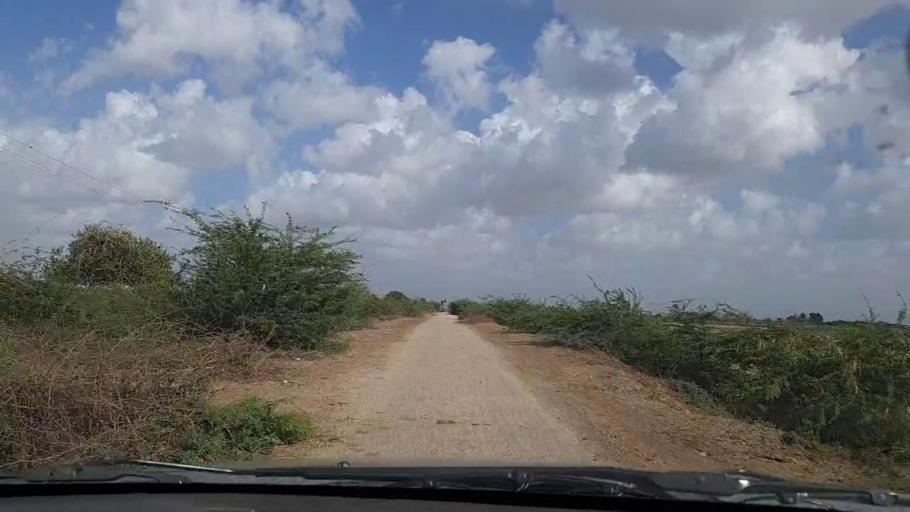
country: PK
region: Sindh
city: Keti Bandar
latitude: 24.0982
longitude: 67.6031
